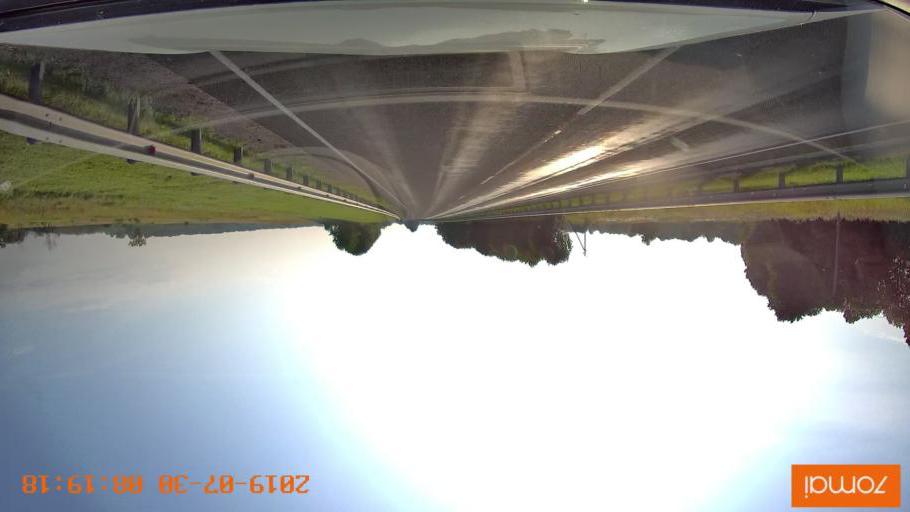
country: RU
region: Kaliningrad
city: Zheleznodorozhnyy
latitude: 54.6291
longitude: 21.4879
